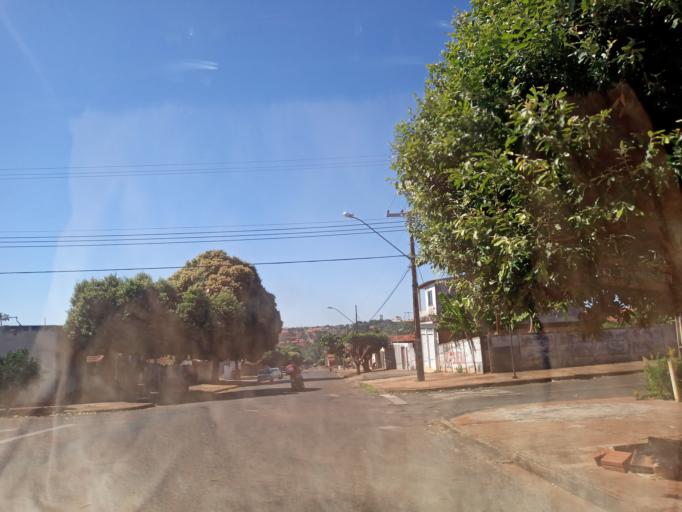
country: BR
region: Minas Gerais
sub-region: Ituiutaba
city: Ituiutaba
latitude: -18.9894
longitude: -49.4468
